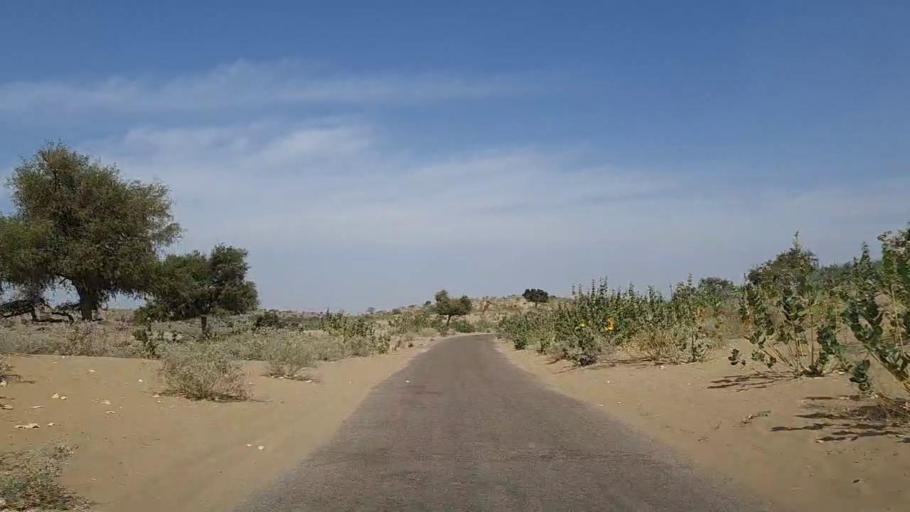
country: PK
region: Sindh
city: Umarkot
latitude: 25.1225
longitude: 70.0023
